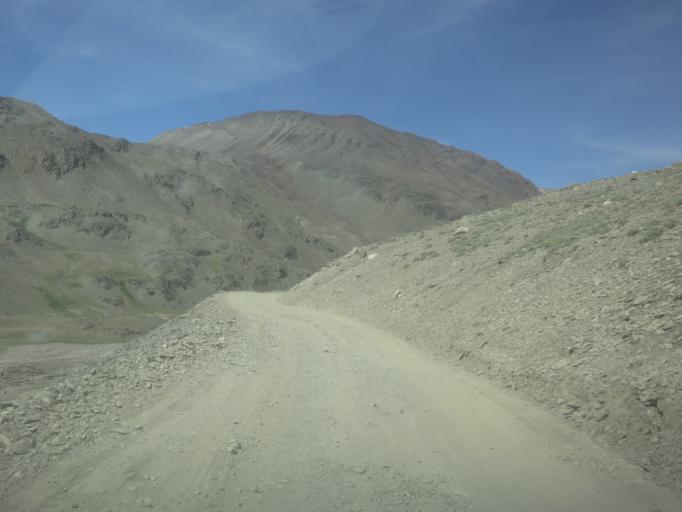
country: IN
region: Himachal Pradesh
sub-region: Kulu
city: Manali
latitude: 32.4096
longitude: 77.6427
